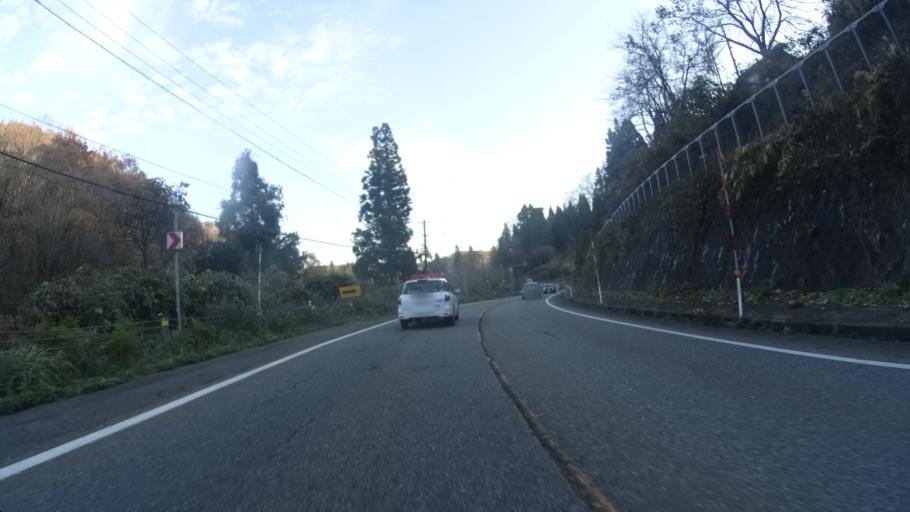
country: JP
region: Niigata
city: Kashiwazaki
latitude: 37.4117
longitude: 138.6848
